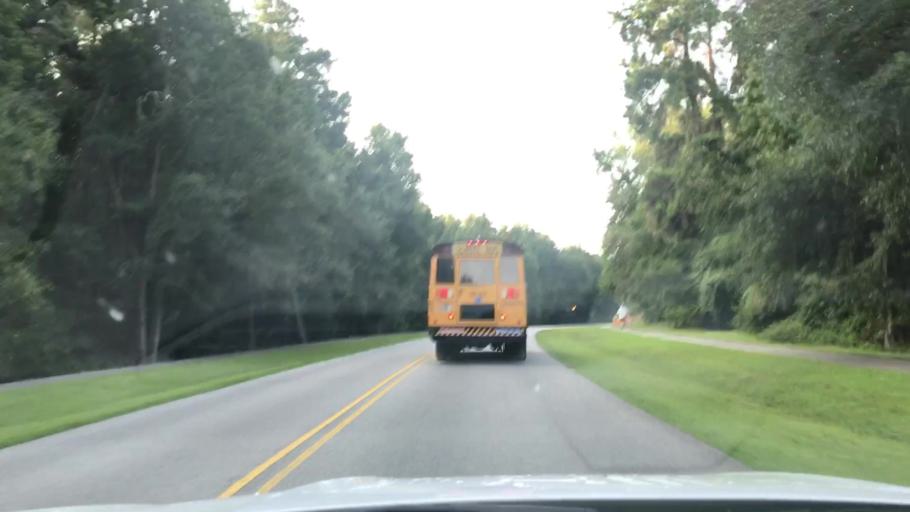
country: US
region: South Carolina
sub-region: Charleston County
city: Shell Point
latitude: 32.8298
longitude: -80.0868
